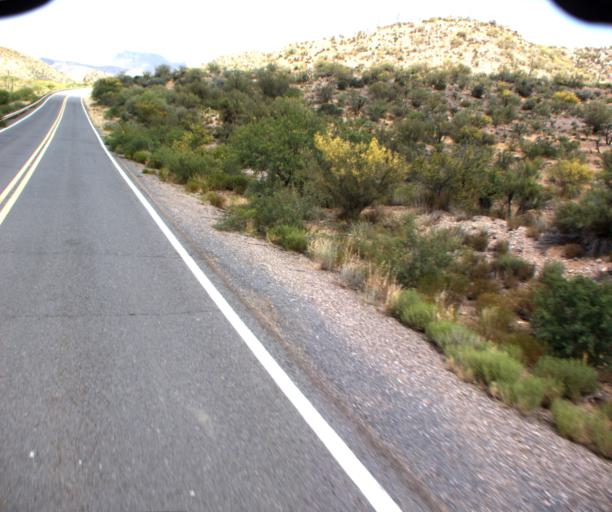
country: US
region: Arizona
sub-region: Pinal County
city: Superior
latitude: 33.2258
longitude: -111.0788
